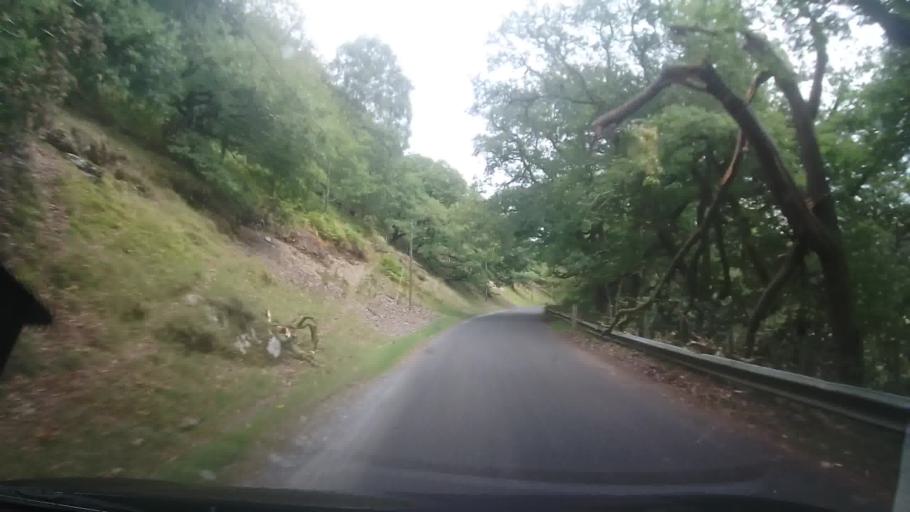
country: GB
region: Wales
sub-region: Sir Powys
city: Rhayader
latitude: 52.3135
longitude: -3.5473
